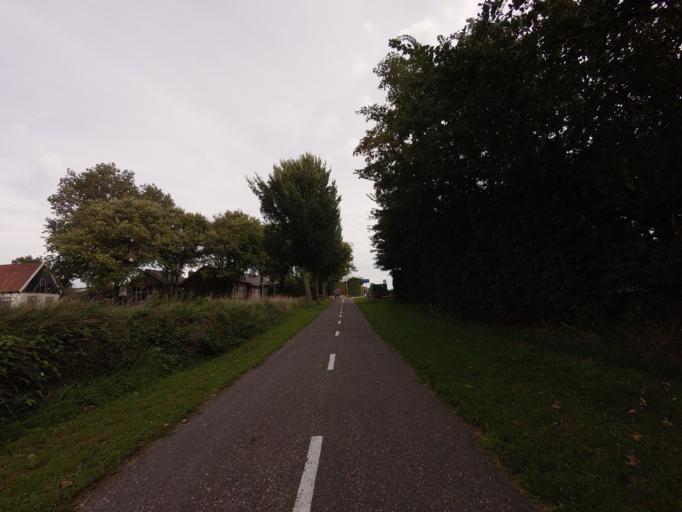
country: NL
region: North Holland
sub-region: Gemeente Texel
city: Den Burg
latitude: 53.0715
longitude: 4.8205
